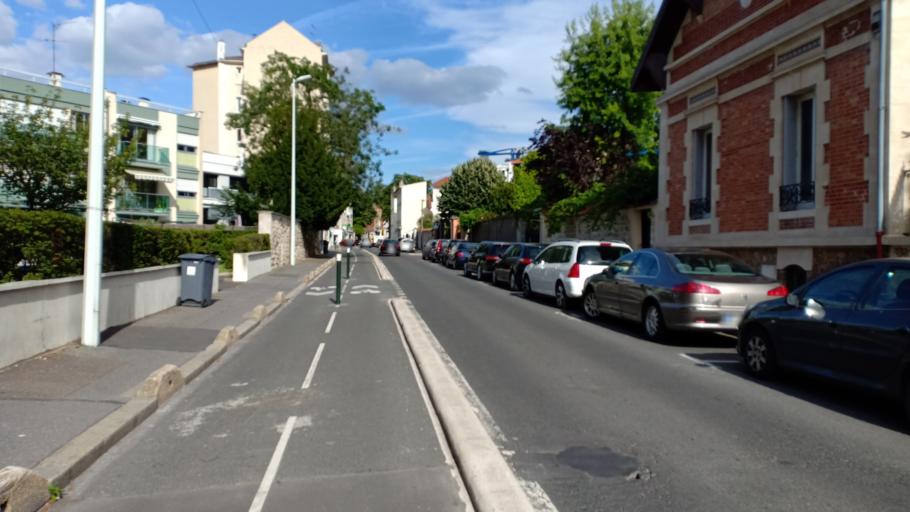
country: FR
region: Ile-de-France
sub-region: Departement des Hauts-de-Seine
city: Nanterre
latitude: 48.8896
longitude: 2.2002
